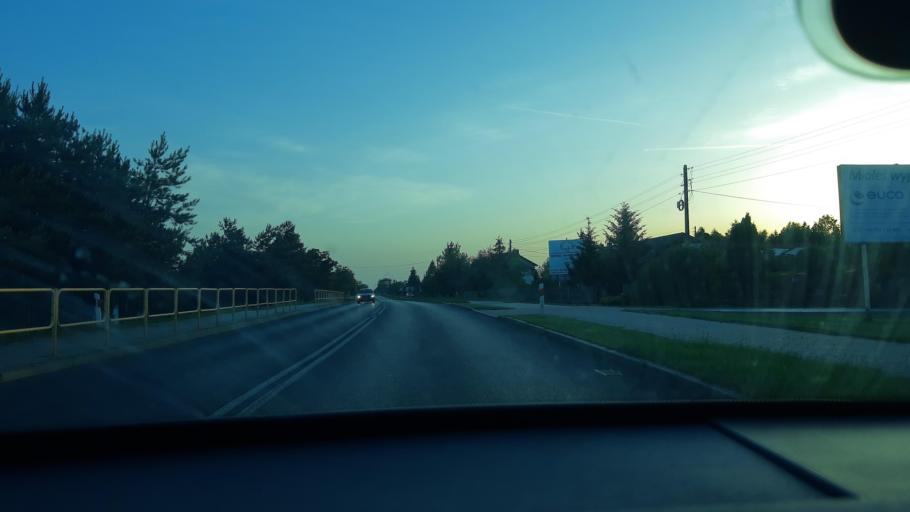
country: PL
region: Lodz Voivodeship
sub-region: Powiat zdunskowolski
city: Zdunska Wola
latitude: 51.6083
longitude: 18.8994
